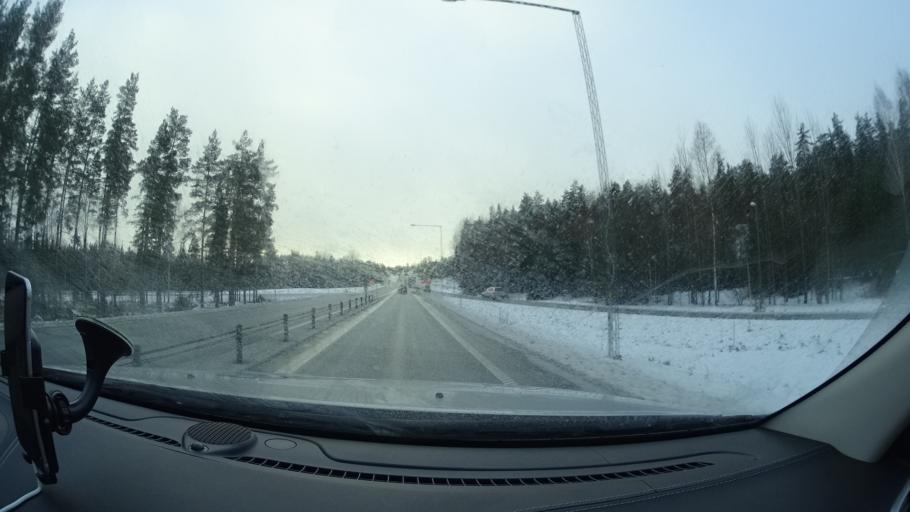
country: SE
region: OErebro
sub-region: Nora Kommun
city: Nora
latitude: 59.4685
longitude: 15.1324
